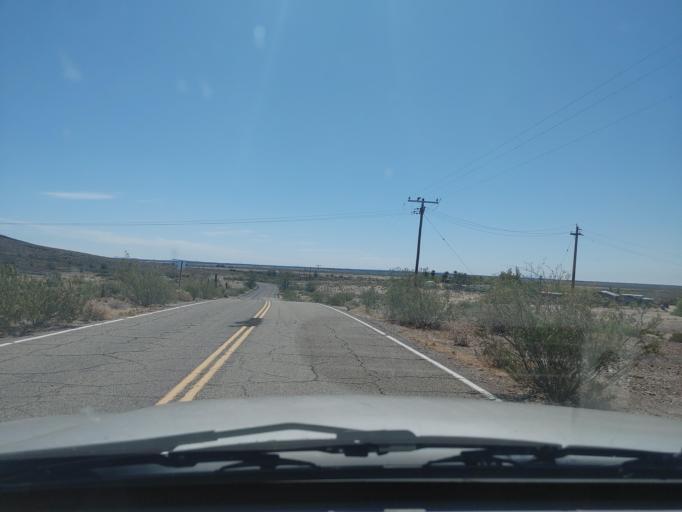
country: US
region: Arizona
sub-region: Maricopa County
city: Gila Bend
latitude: 32.9897
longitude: -113.3348
